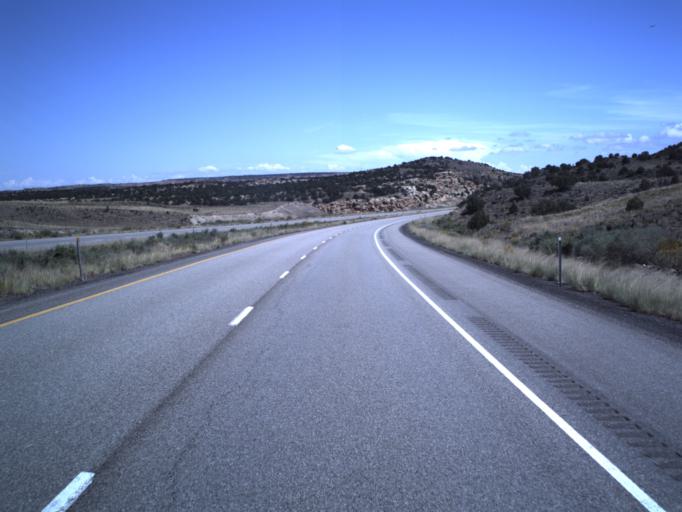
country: US
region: Utah
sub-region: Emery County
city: Ferron
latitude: 38.7961
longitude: -111.2870
